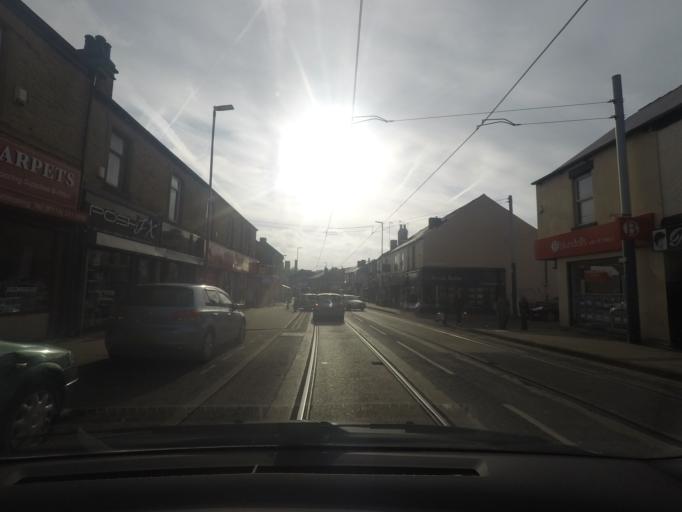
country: GB
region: England
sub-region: Sheffield
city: Sheffield
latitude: 53.4038
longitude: -1.5031
